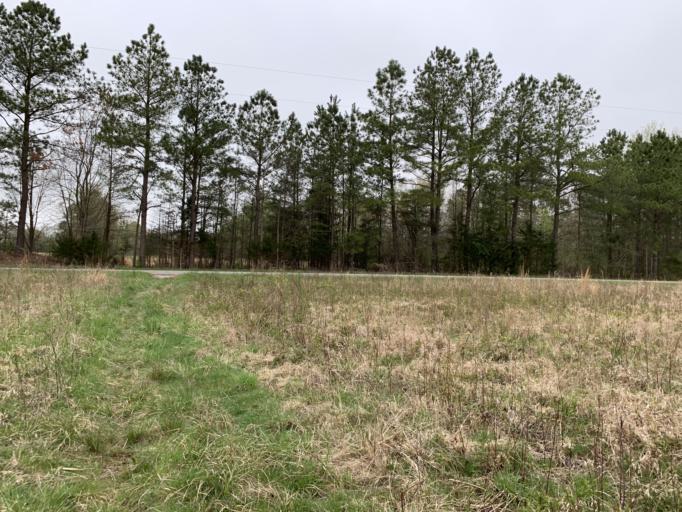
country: US
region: Delaware
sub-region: Kent County
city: Felton
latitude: 39.0358
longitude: -75.6436
